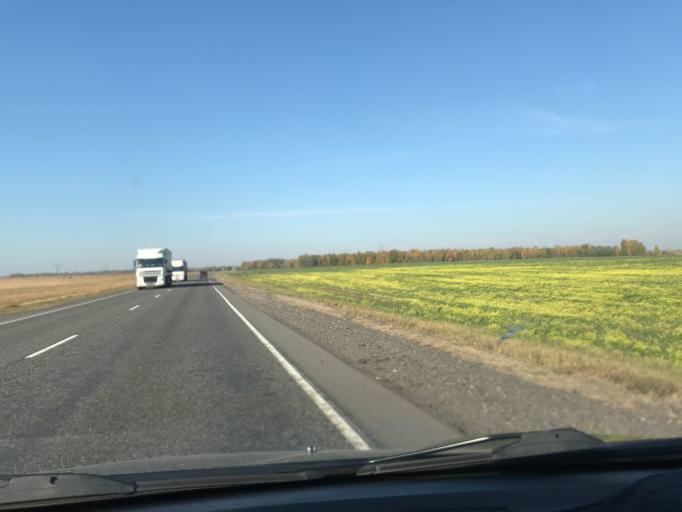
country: BY
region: Mogilev
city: Babruysk
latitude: 53.0901
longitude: 29.0618
